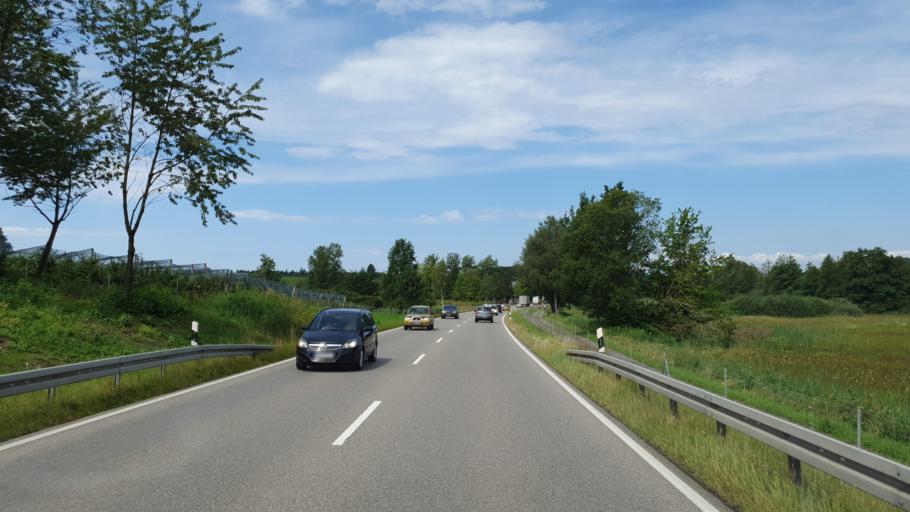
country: DE
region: Bavaria
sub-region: Swabia
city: Bodolz
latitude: 47.5830
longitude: 9.6663
